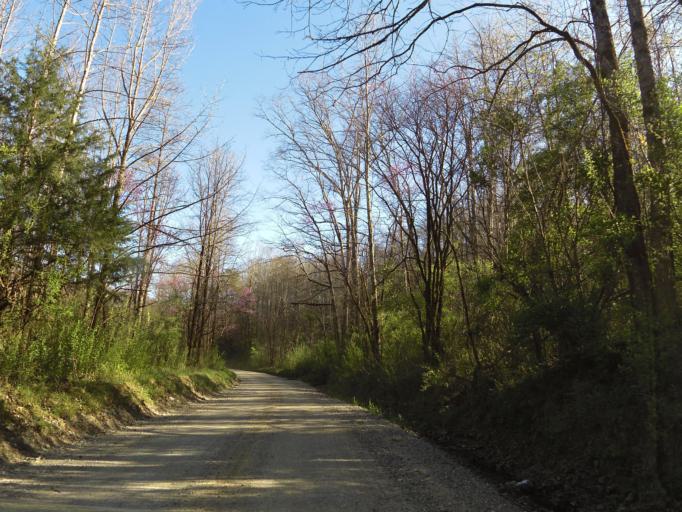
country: US
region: Tennessee
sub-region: Campbell County
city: Caryville
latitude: 36.2528
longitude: -84.3954
